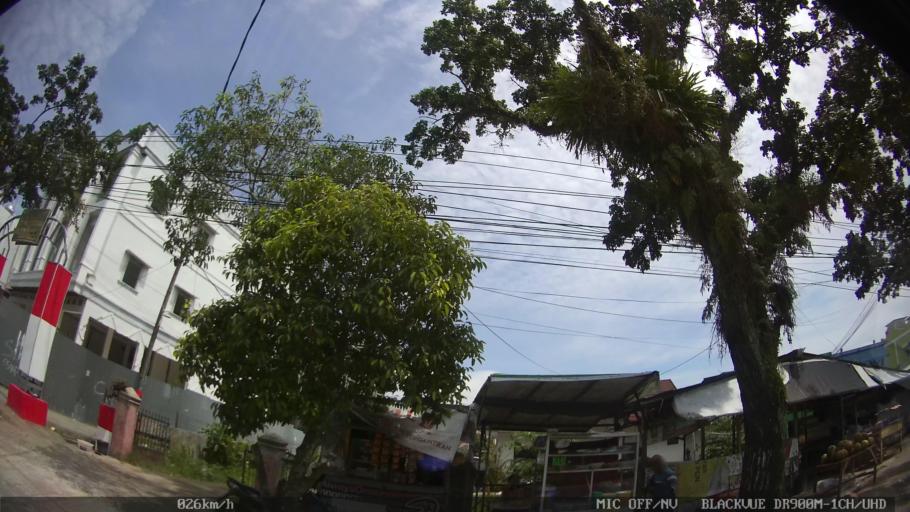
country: ID
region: North Sumatra
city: Sunggal
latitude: 3.5809
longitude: 98.6376
